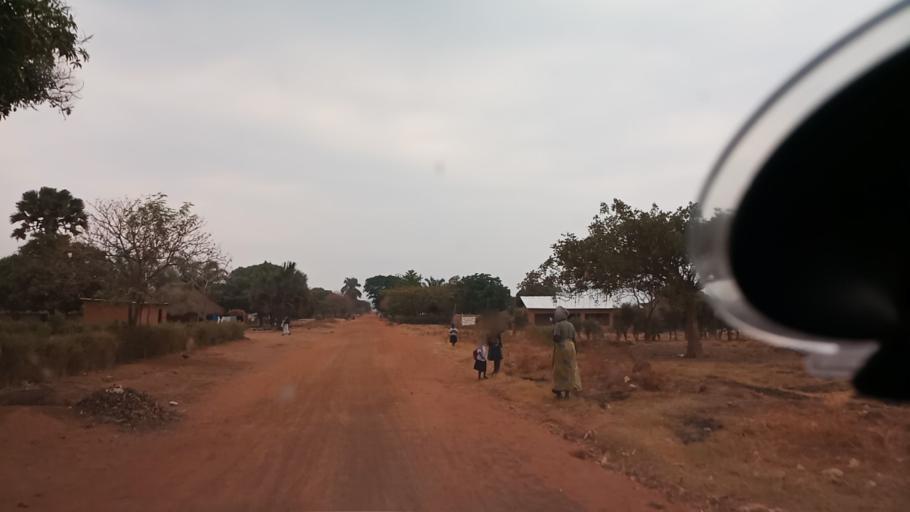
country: ZM
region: Luapula
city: Nchelenge
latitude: -9.2769
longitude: 28.3283
